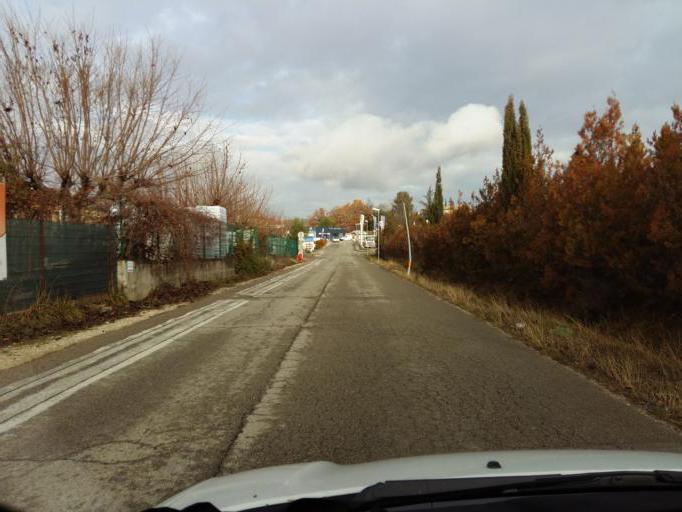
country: FR
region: Provence-Alpes-Cote d'Azur
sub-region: Departement du Vaucluse
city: Vaison-la-Romaine
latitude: 44.2431
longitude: 5.0892
